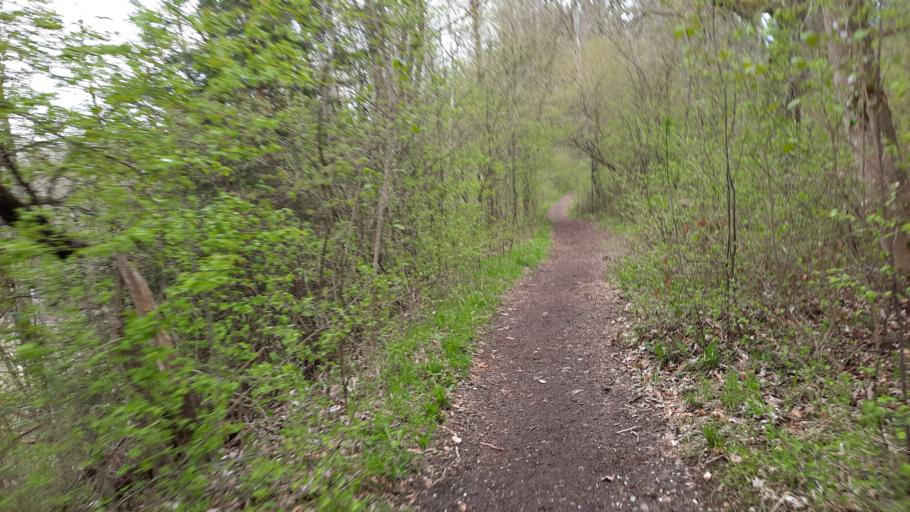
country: DE
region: Bavaria
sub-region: Swabia
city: Buxheim
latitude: 47.9891
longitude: 10.1294
